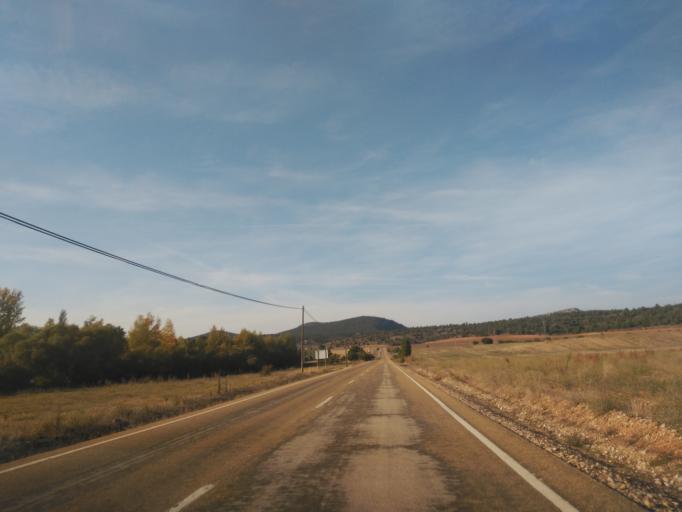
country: ES
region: Castille and Leon
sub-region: Provincia de Soria
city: Ucero
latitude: 41.7032
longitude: -3.0449
